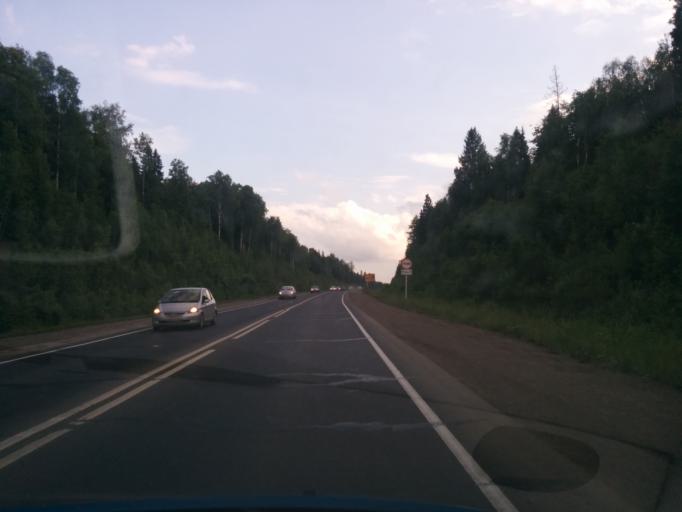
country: RU
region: Perm
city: Novyye Lyady
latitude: 58.0832
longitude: 56.4302
